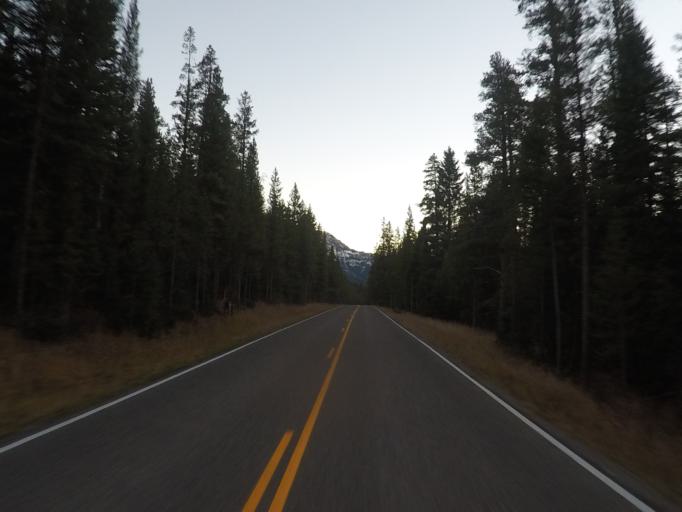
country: US
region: Montana
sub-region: Stillwater County
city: Absarokee
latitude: 44.9637
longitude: -110.0705
